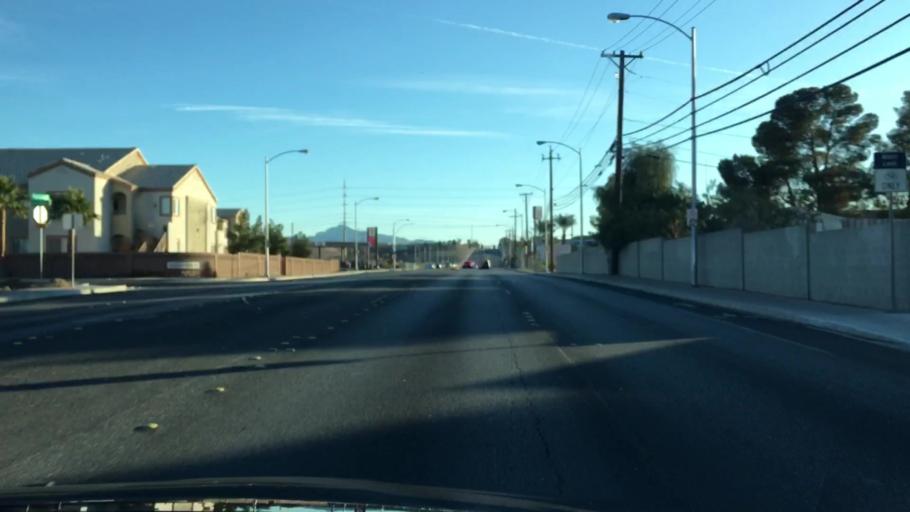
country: US
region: Nevada
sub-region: Clark County
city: Whitney
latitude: 36.0878
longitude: -115.0732
